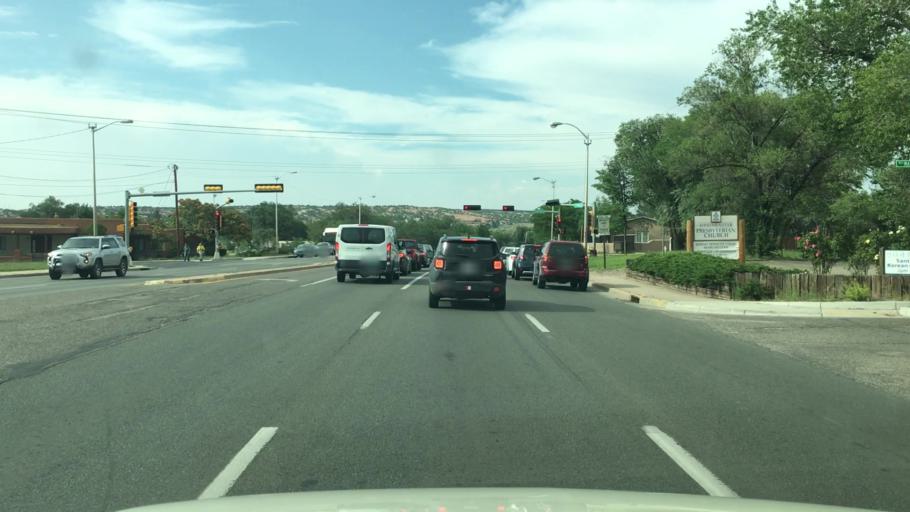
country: US
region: New Mexico
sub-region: Santa Fe County
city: Santa Fe
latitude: 35.6835
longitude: -105.9548
